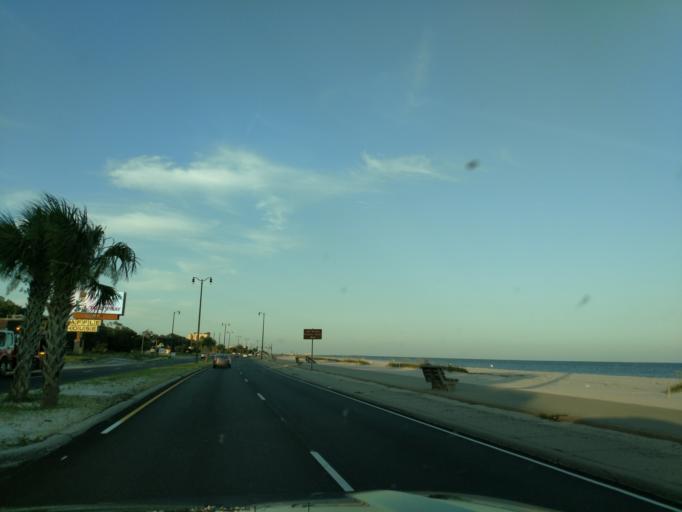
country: US
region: Mississippi
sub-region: Harrison County
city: Gulfport
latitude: 30.3795
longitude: -89.0402
